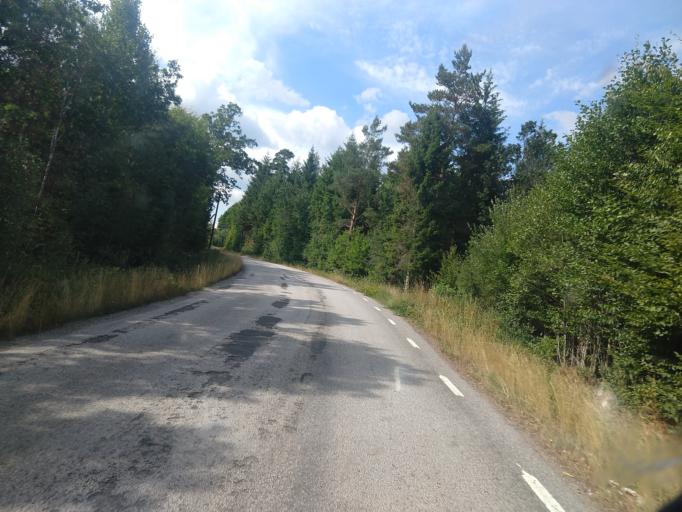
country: SE
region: Blekinge
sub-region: Karlskrona Kommun
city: Rodeby
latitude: 56.2349
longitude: 15.5763
